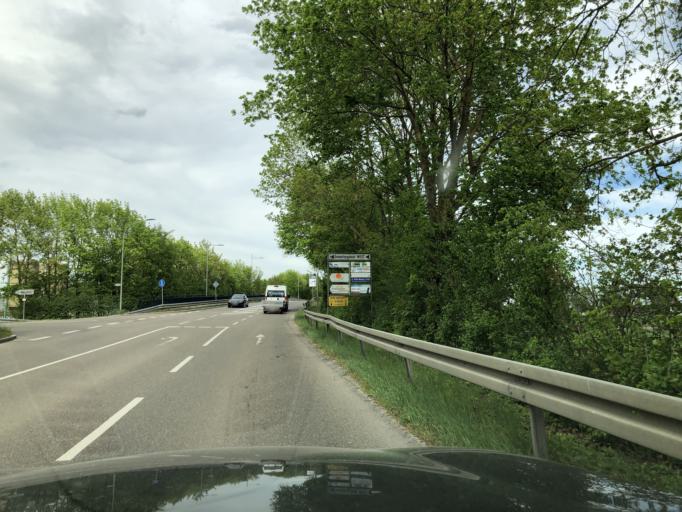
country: DE
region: Bavaria
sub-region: Swabia
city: Asbach-Baumenheim
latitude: 48.6719
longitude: 10.8145
